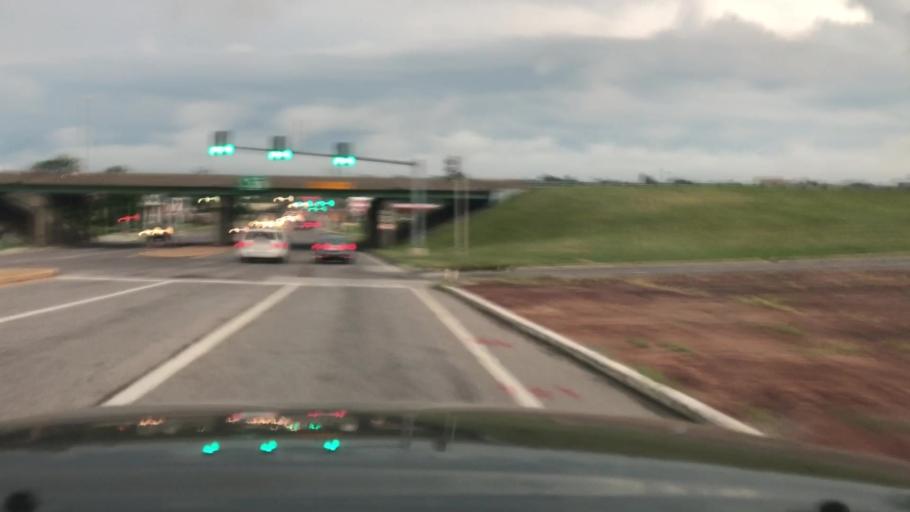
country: US
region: Missouri
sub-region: Saint Louis County
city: Saint Ann
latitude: 38.7381
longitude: -90.3999
